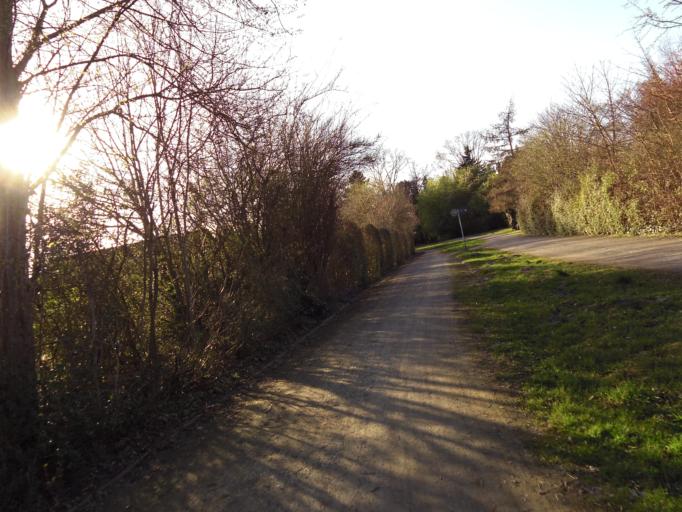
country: DE
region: Lower Saxony
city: Laatzen
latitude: 52.3758
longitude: 9.8162
